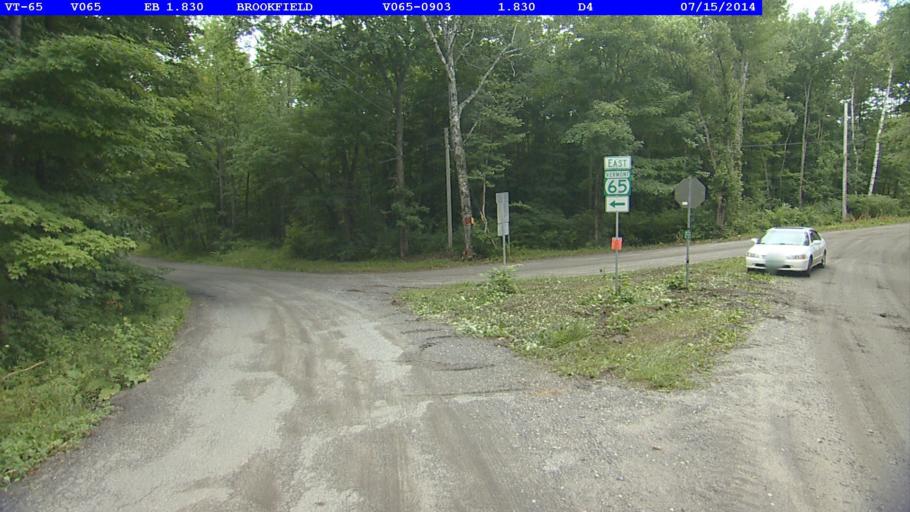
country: US
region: Vermont
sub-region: Washington County
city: Northfield
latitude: 44.0445
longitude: -72.6256
